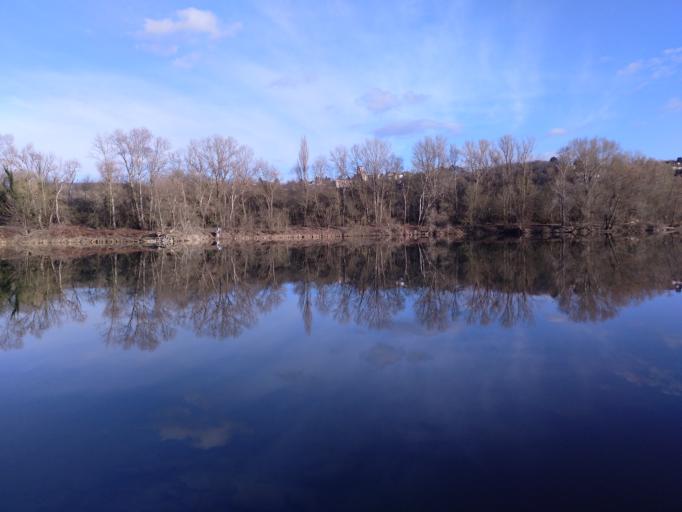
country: FR
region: Rhone-Alpes
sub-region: Departement du Rhone
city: Grigny
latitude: 45.6125
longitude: 4.8007
